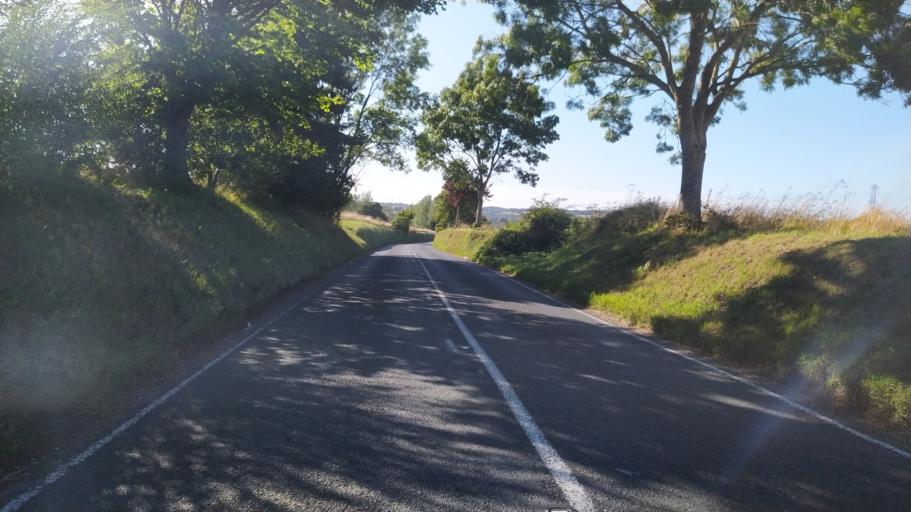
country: GB
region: England
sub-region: Hampshire
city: Alton
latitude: 51.1384
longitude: -0.9399
